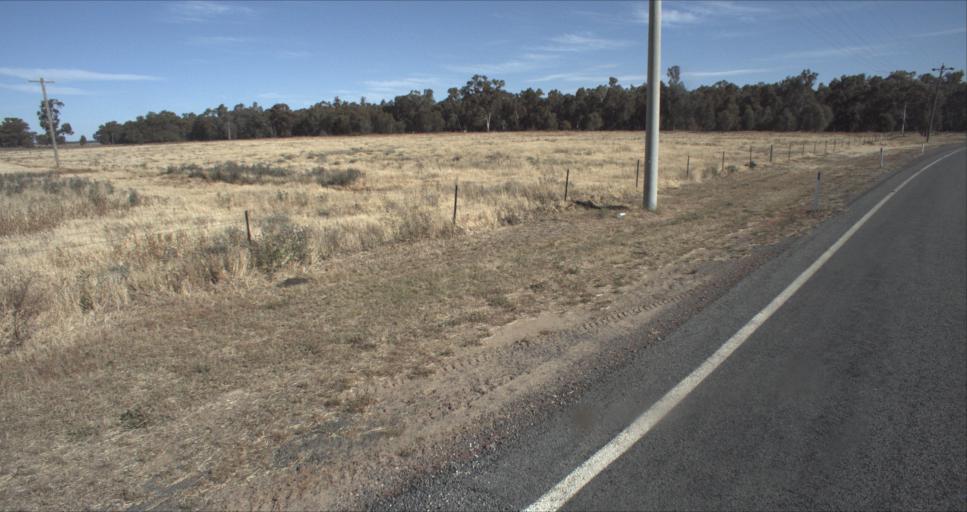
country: AU
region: New South Wales
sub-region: Leeton
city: Leeton
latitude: -34.6243
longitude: 146.3950
